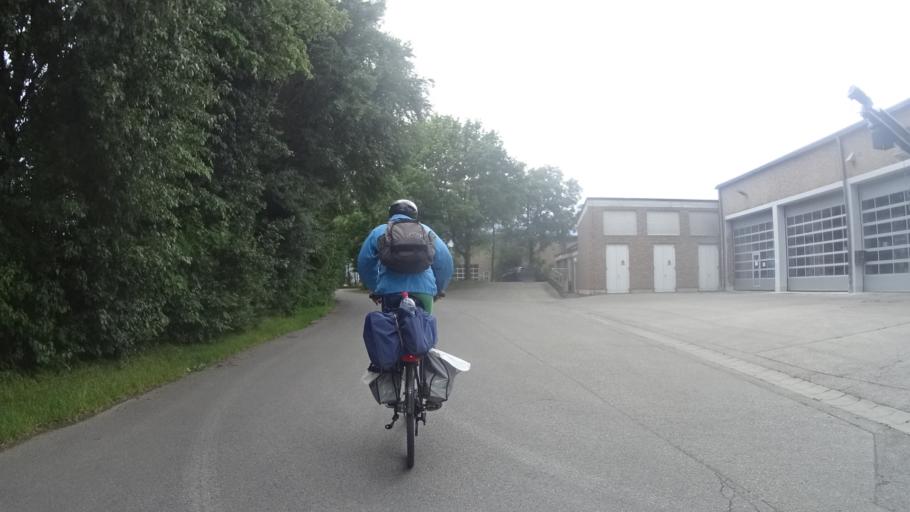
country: DE
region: Bavaria
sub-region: Upper Bavaria
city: Bergkirchen
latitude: 48.2334
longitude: 11.3621
